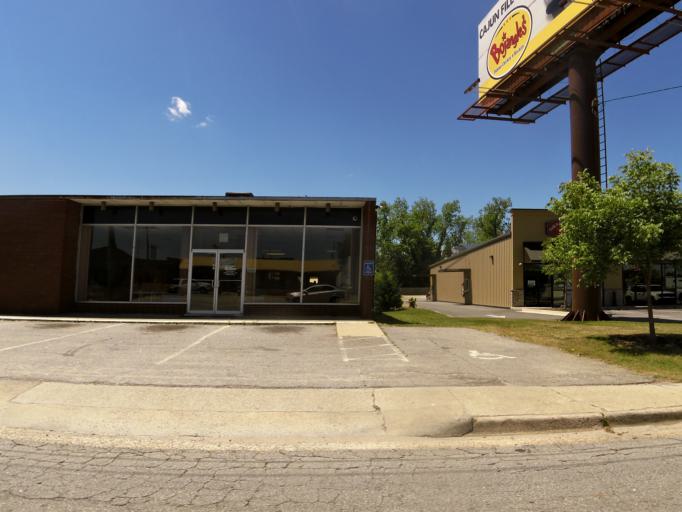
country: US
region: Georgia
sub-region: Richmond County
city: Augusta
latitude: 33.4699
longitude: -81.9737
